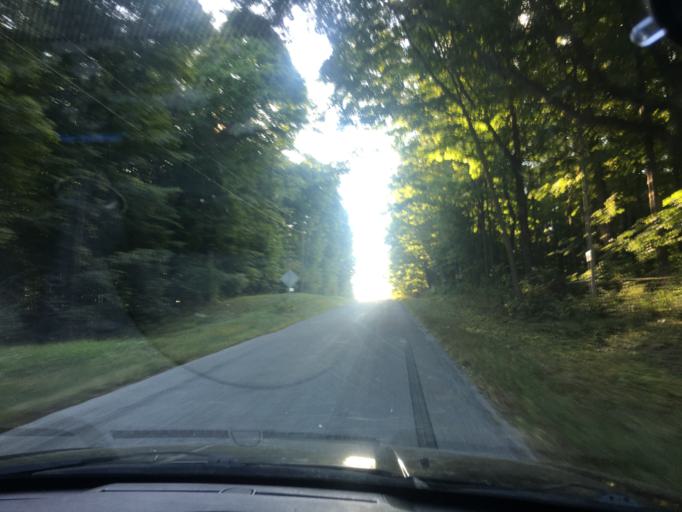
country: US
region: Ohio
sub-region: Champaign County
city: Urbana
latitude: 40.1712
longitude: -83.7660
